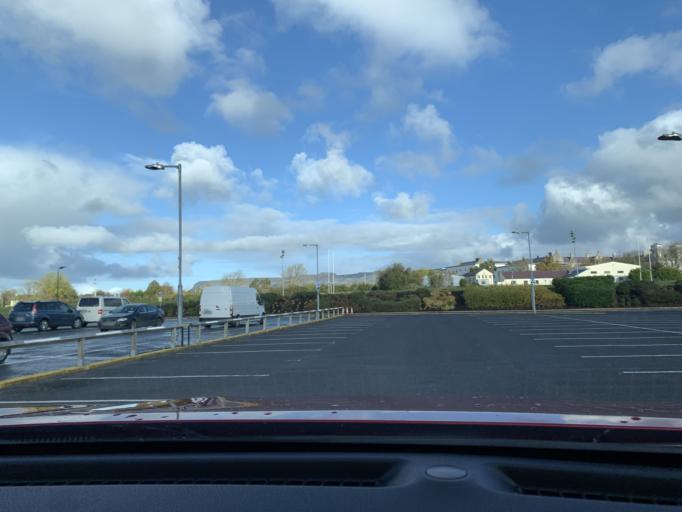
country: IE
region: Connaught
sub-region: Sligo
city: Sligo
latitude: 54.2790
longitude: -8.4644
